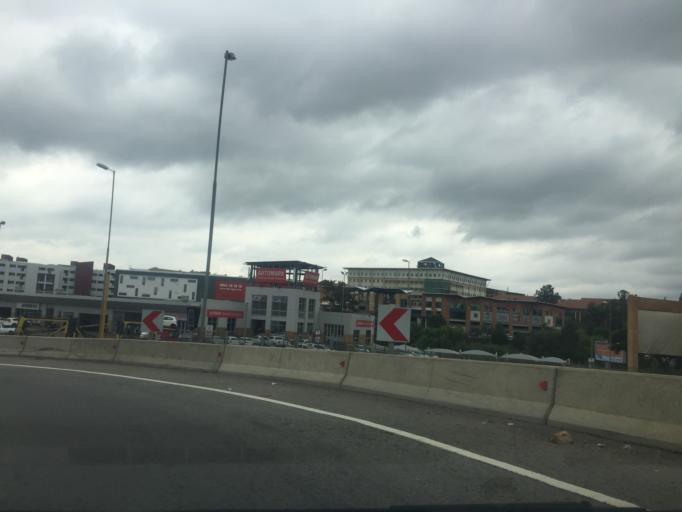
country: ZA
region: Gauteng
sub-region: City of Johannesburg Metropolitan Municipality
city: Midrand
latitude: -26.0381
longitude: 28.0628
